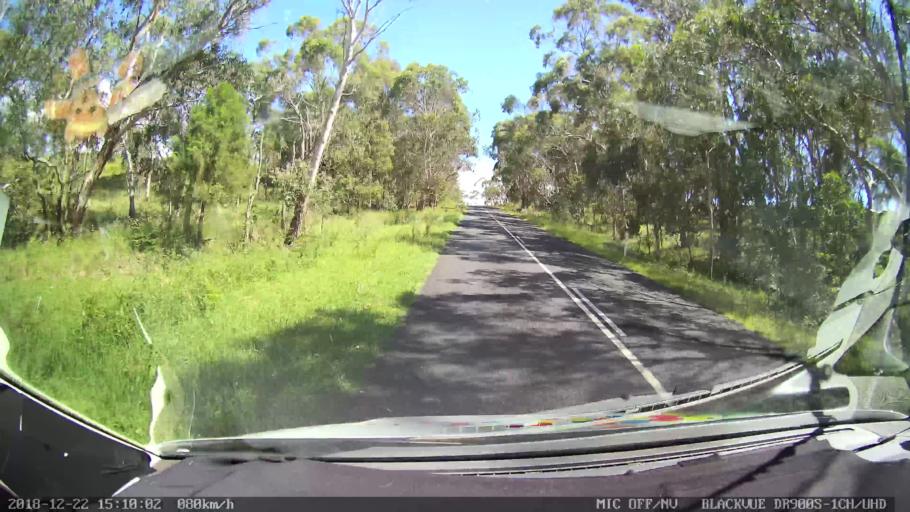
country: AU
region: New South Wales
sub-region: Bellingen
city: Dorrigo
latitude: -30.3305
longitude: 152.4056
